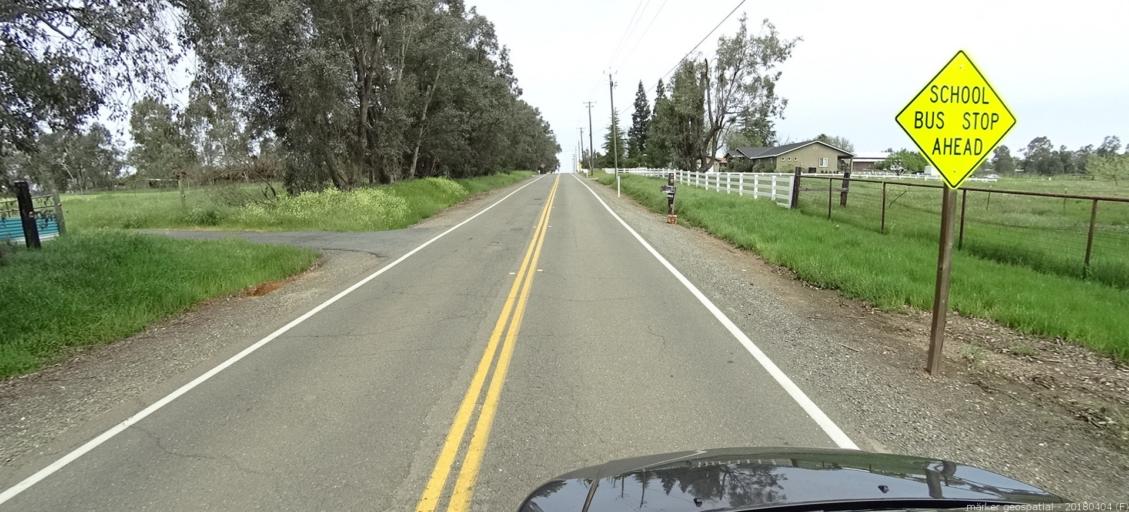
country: US
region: California
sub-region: Sacramento County
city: Clay
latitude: 38.3182
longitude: -121.1713
